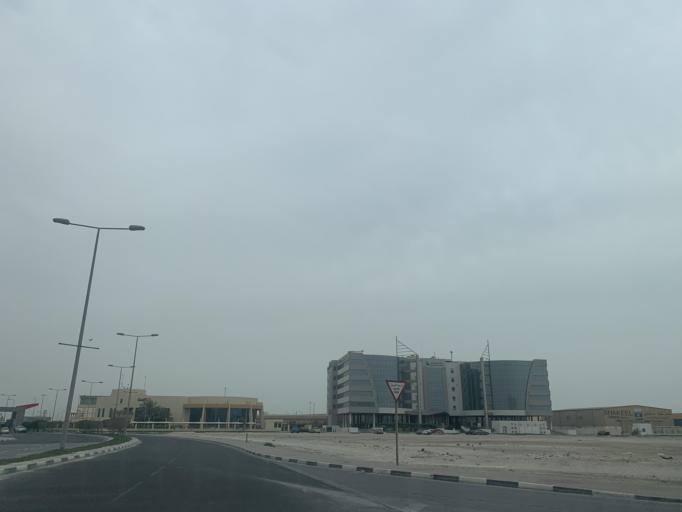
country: BH
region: Muharraq
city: Al Hadd
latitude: 26.2134
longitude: 50.6700
